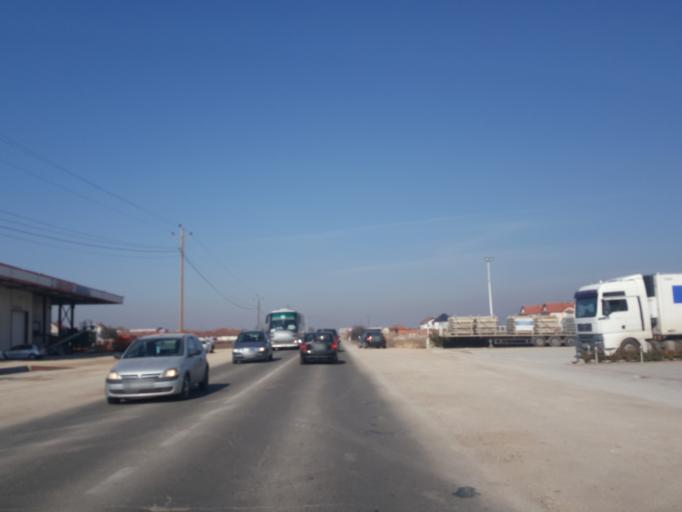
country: XK
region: Mitrovica
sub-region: Vushtrri
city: Vushtrri
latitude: 42.7843
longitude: 21.0102
